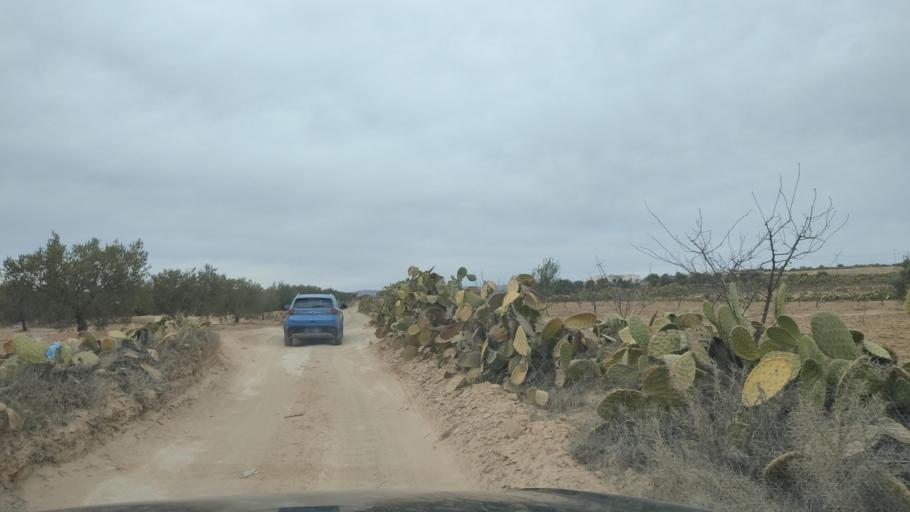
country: TN
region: Al Qasrayn
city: Kasserine
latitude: 35.2276
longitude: 8.9156
